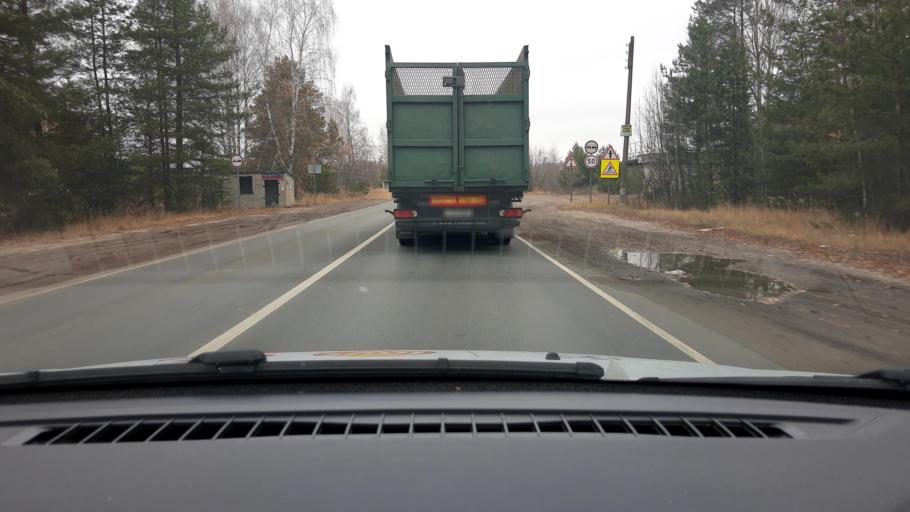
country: RU
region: Nizjnij Novgorod
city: Gorodets
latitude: 56.5668
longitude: 43.4850
